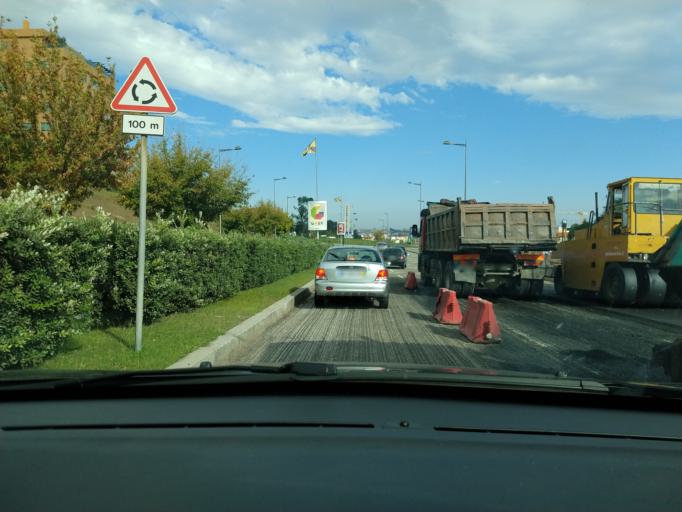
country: PT
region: Porto
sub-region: Vila Nova de Gaia
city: Oliveira do Douro
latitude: 41.1238
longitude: -8.5984
